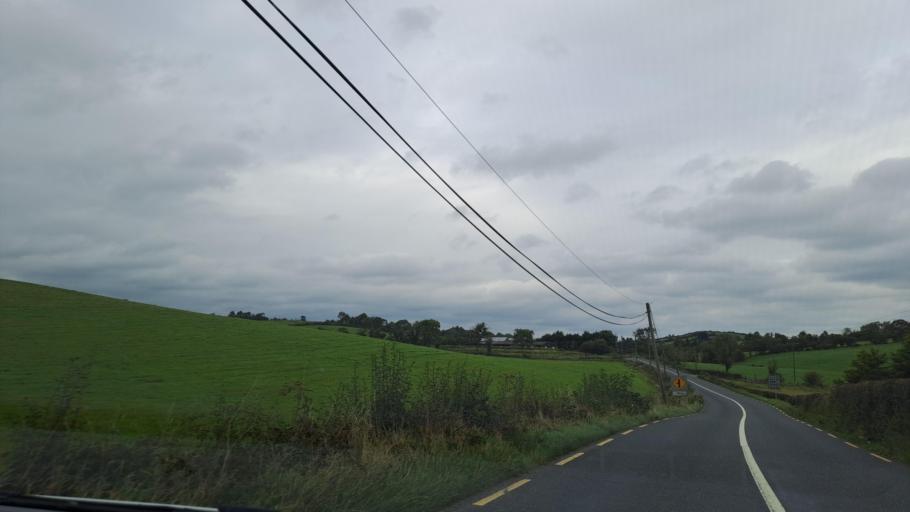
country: IE
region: Ulster
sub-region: An Cabhan
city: Bailieborough
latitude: 53.9336
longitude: -6.9657
